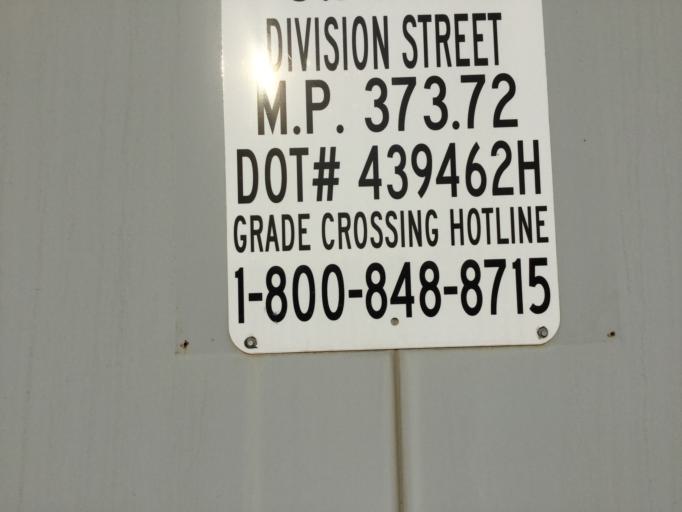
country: US
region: Kansas
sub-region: Coffey County
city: Burlington
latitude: 38.1801
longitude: -95.4902
